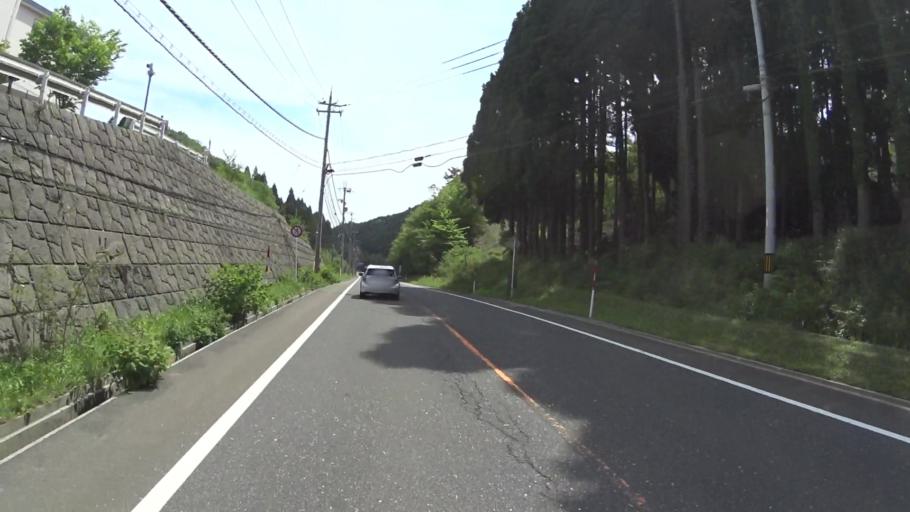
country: JP
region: Fukui
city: Obama
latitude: 35.3949
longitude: 135.9294
